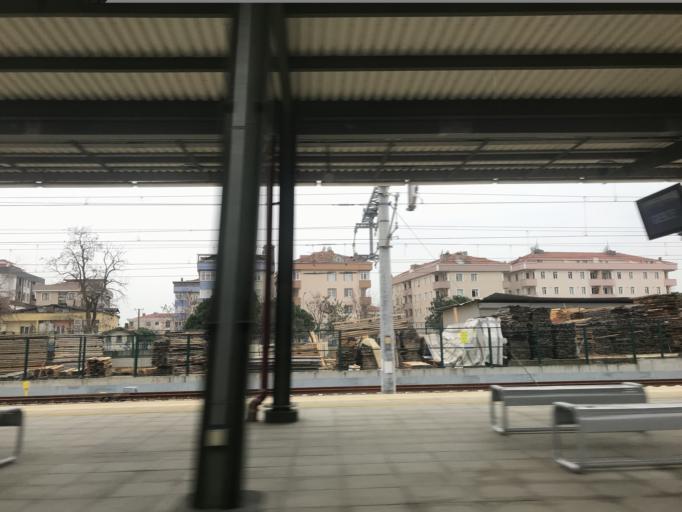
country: TR
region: Istanbul
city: Icmeler
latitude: 40.8295
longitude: 29.3229
